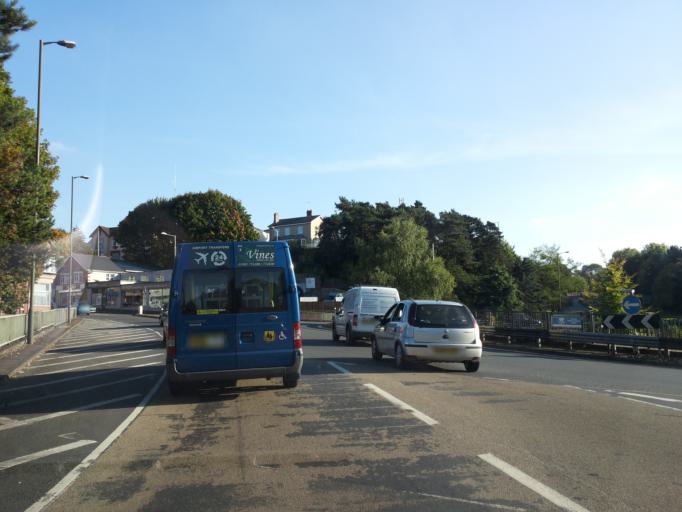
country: GB
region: England
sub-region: Worcestershire
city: Kidderminster
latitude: 52.3862
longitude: -2.2439
